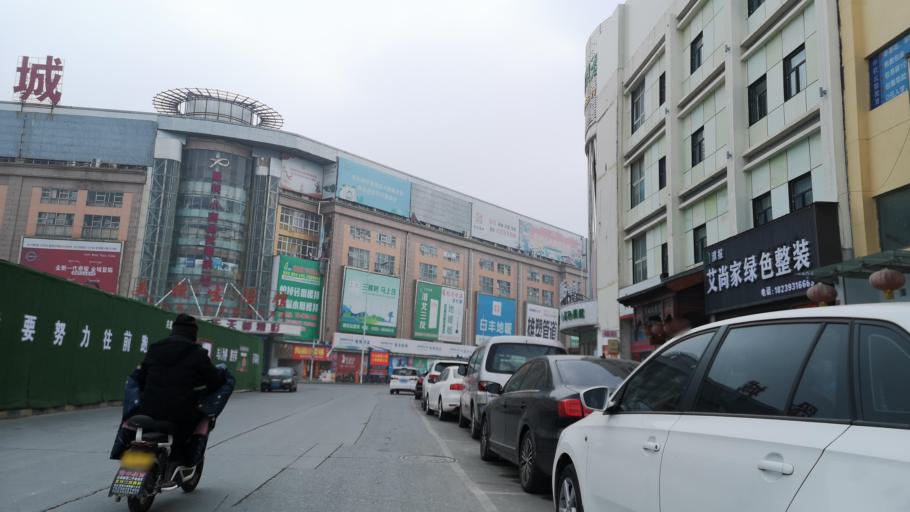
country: CN
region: Henan Sheng
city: Zhongyuanlu
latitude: 35.7747
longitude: 115.0535
